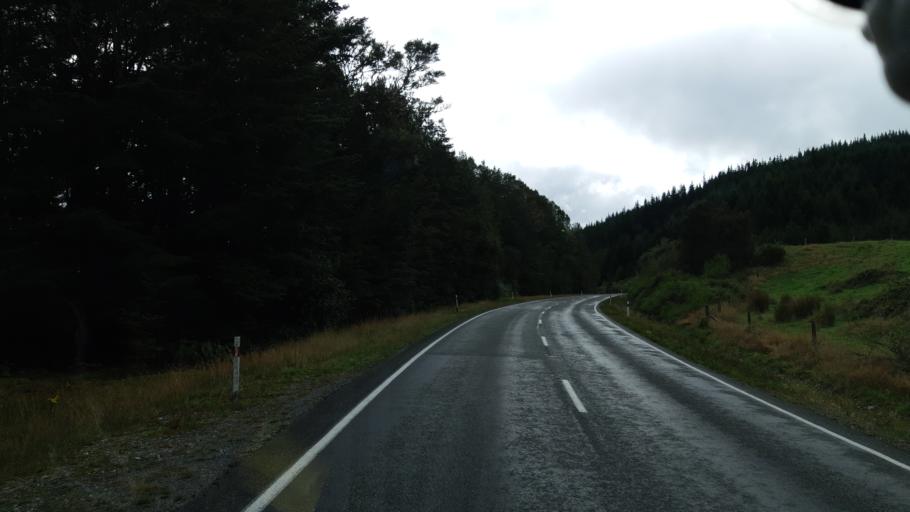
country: NZ
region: West Coast
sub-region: Buller District
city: Westport
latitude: -41.9183
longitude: 172.2249
